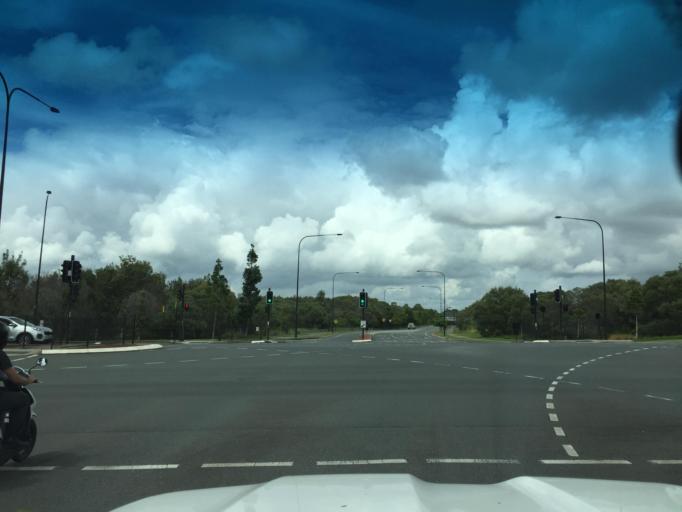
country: AU
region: Queensland
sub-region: Moreton Bay
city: Mango Hill
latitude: -27.2313
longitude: 153.0282
